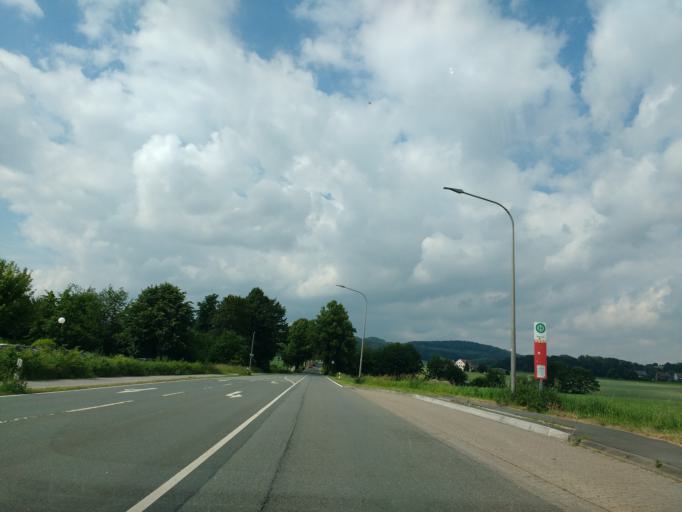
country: DE
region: North Rhine-Westphalia
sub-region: Regierungsbezirk Detmold
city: Lemgo
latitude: 52.0522
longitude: 8.9073
